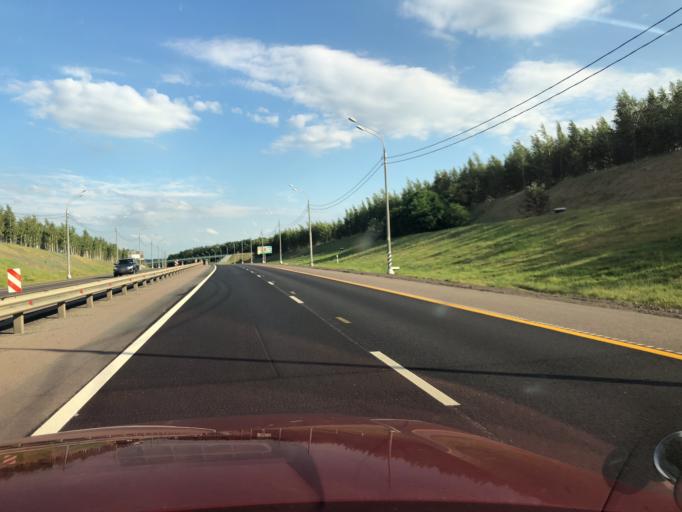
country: RU
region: Lipetsk
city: Zadonsk
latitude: 52.3898
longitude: 38.8648
